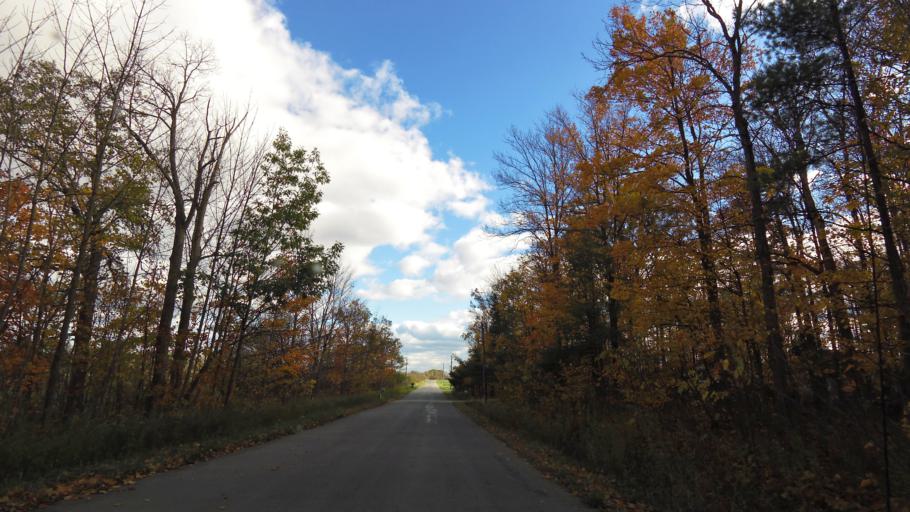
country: CA
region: Ontario
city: Burlington
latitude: 43.4448
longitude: -79.8490
